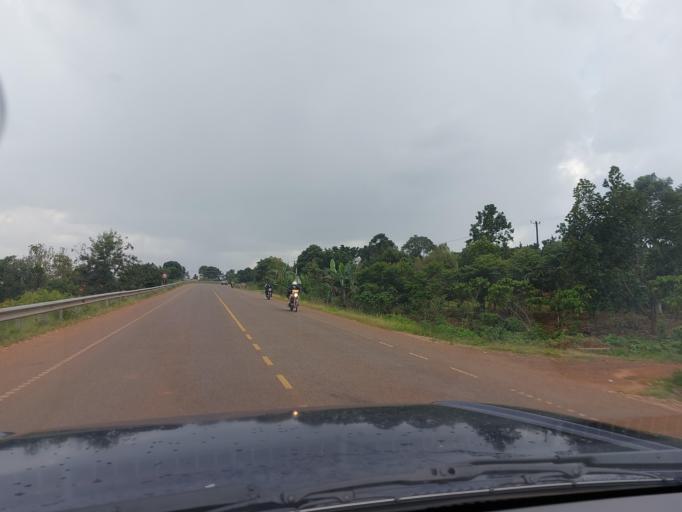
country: UG
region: Central Region
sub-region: Buikwe District
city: Buikwe
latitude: 0.2400
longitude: 32.9290
